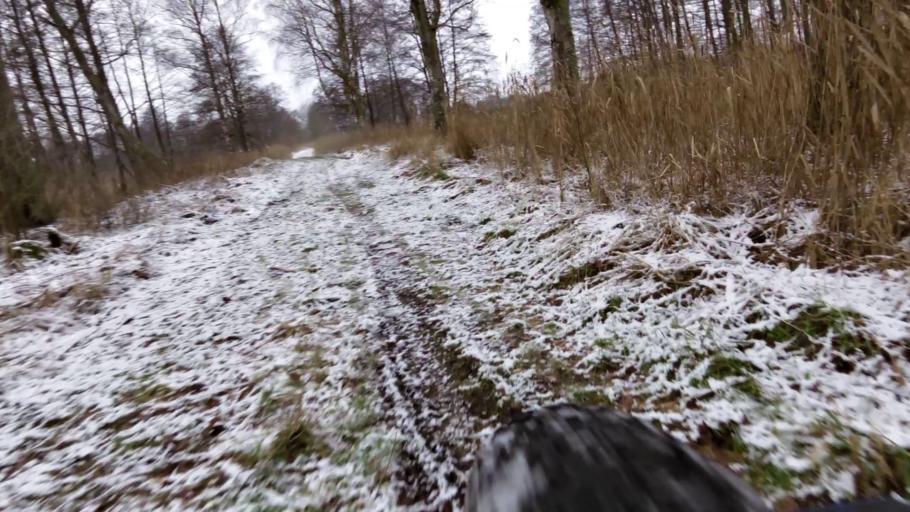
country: PL
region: West Pomeranian Voivodeship
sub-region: Powiat walecki
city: Miroslawiec
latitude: 53.3392
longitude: 16.0999
